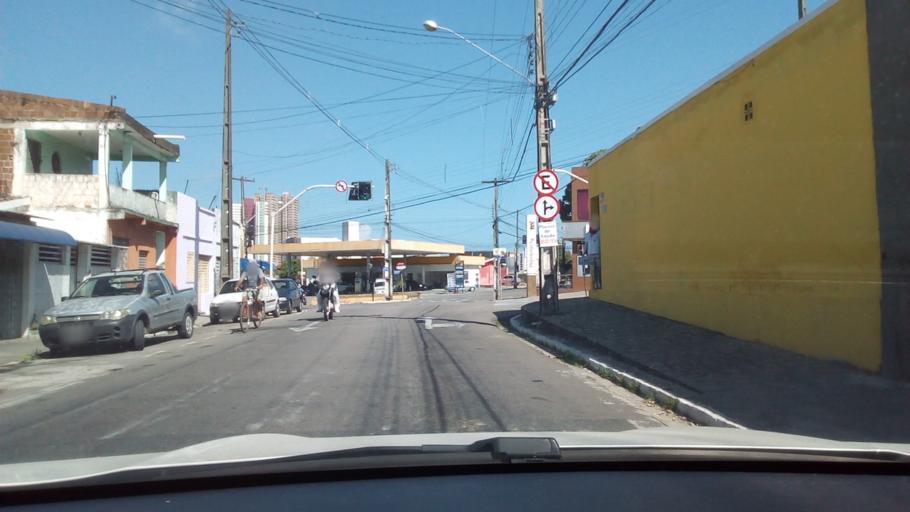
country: BR
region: Paraiba
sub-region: Joao Pessoa
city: Joao Pessoa
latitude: -7.1152
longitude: -34.8747
